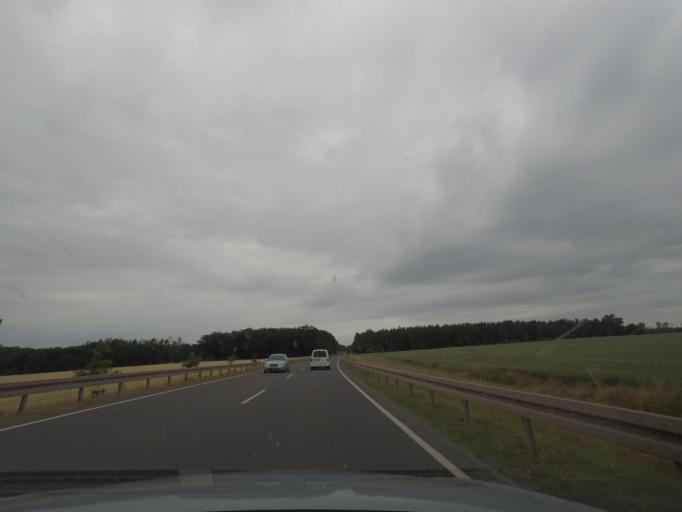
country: DE
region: Saxony-Anhalt
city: Suplingen
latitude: 52.2484
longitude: 11.3484
